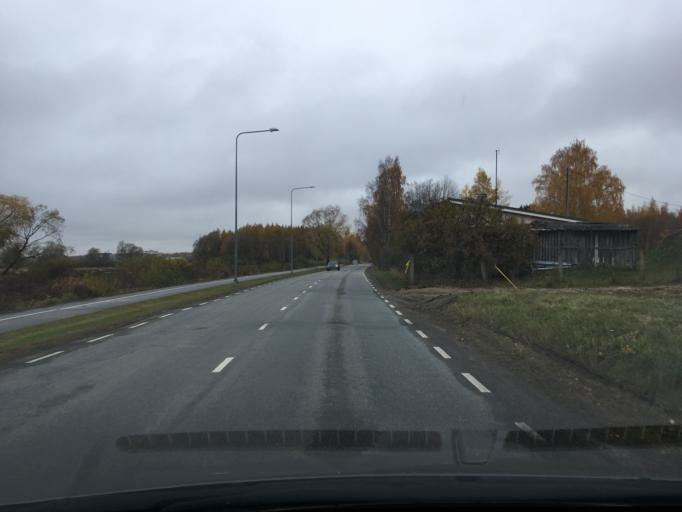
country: EE
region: Tartu
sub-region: Tartu linn
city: Tartu
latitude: 58.3636
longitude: 26.7589
